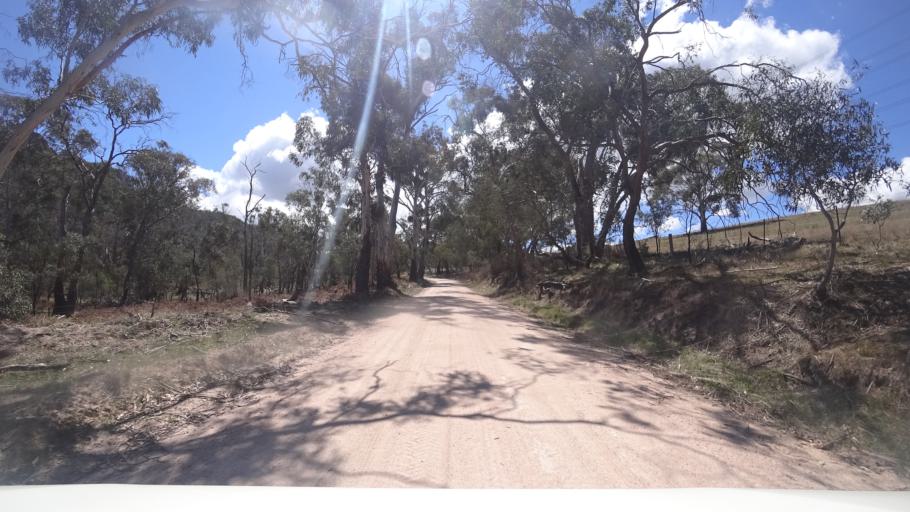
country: AU
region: New South Wales
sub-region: Oberon
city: Oberon
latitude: -33.5488
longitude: 149.9315
